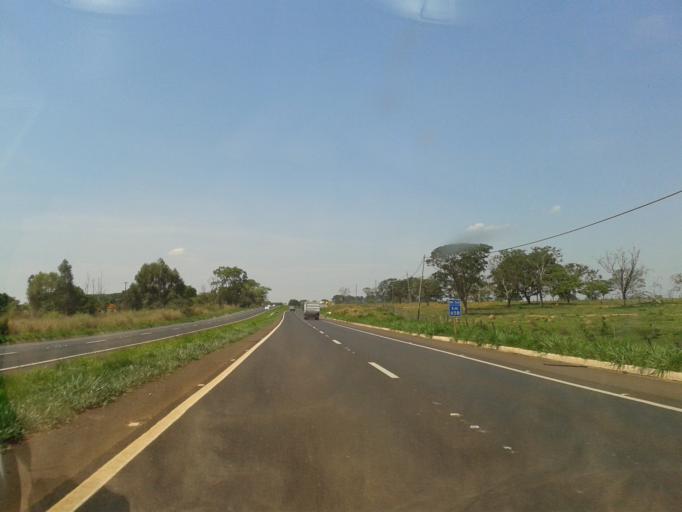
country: BR
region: Minas Gerais
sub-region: Monte Alegre De Minas
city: Monte Alegre de Minas
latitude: -18.8771
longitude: -48.6032
